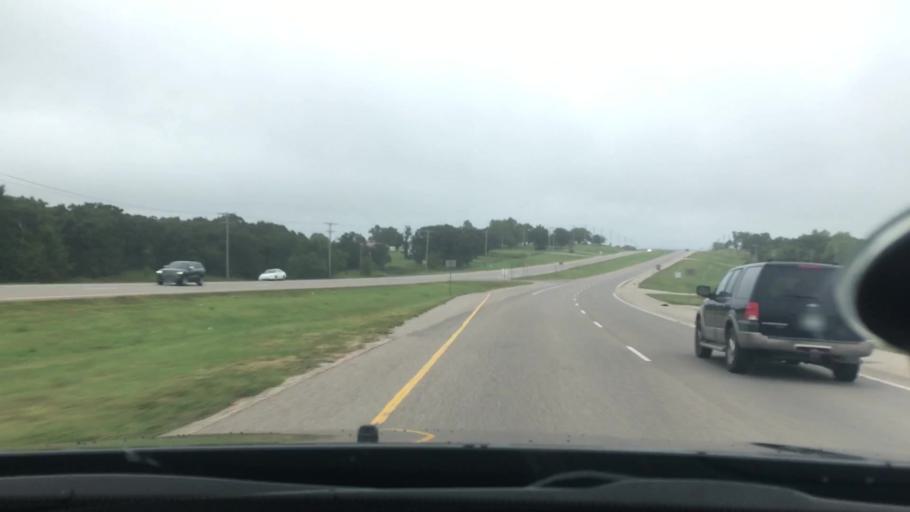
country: US
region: Oklahoma
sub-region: Seminole County
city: Seminole
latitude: 35.3098
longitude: -96.6711
